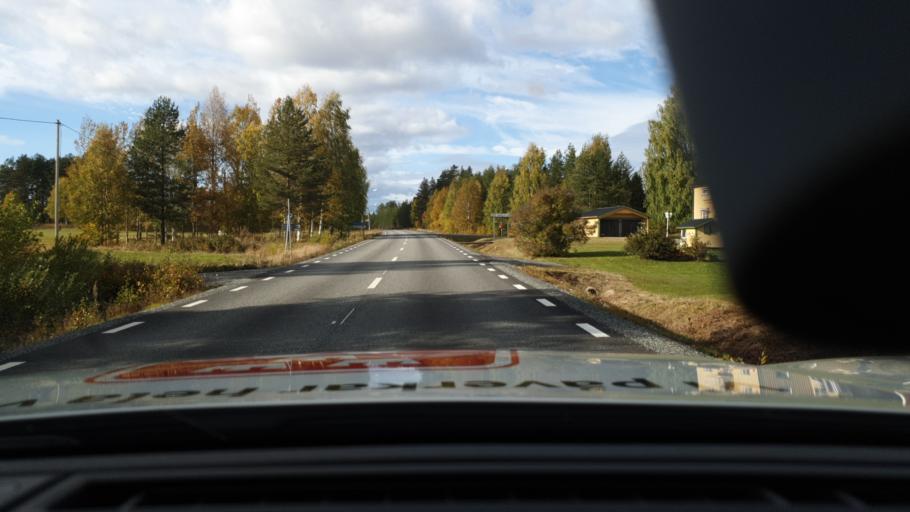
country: SE
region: Vaesterbotten
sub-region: Mala Kommun
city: Mala
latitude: 64.9064
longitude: 18.6819
